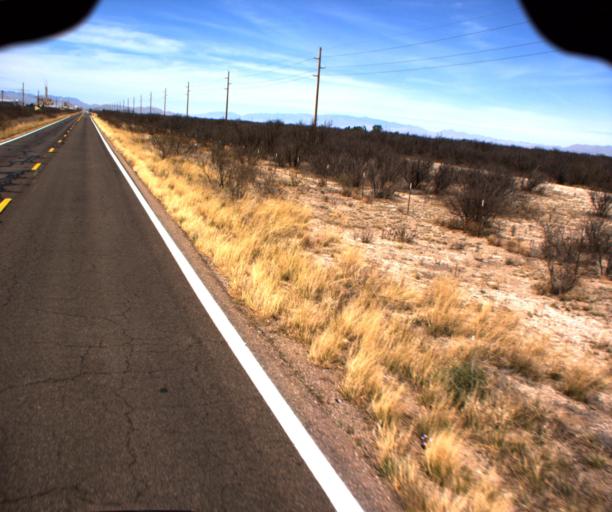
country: US
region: Arizona
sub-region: Cochise County
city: Willcox
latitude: 32.0297
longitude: -109.8758
